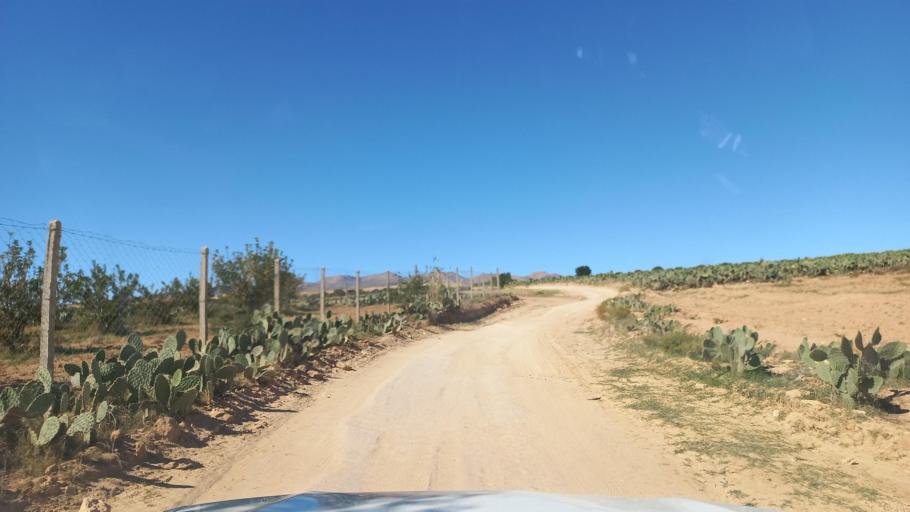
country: TN
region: Al Qasrayn
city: Sbiba
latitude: 35.3729
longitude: 9.0933
